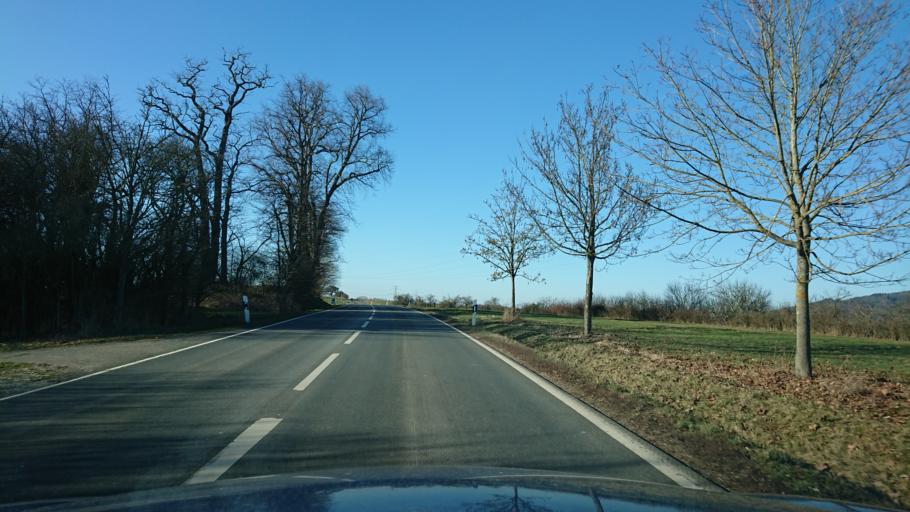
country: DE
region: Bavaria
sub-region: Upper Franconia
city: Neunkirchen am Brand
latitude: 49.6218
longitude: 11.1240
